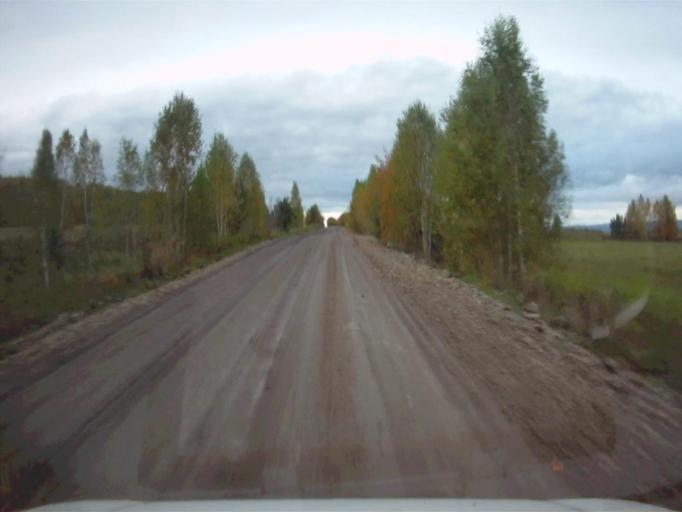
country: RU
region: Sverdlovsk
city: Mikhaylovsk
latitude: 56.1973
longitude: 59.1996
